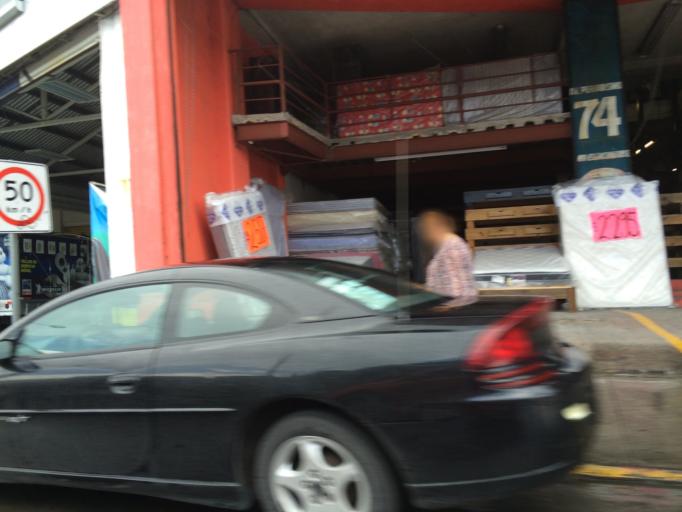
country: MX
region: Michoacan
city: Morelia
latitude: 19.7015
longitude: -101.2132
